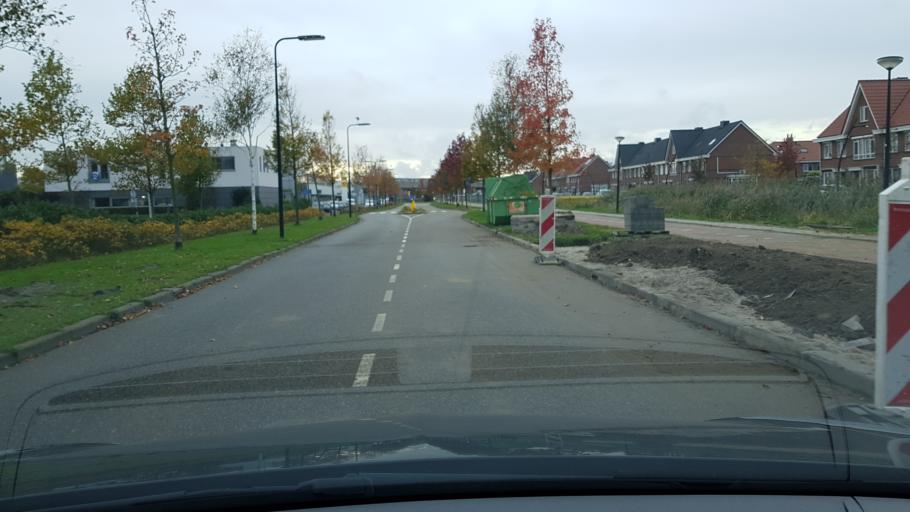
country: NL
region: South Holland
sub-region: Gemeente Spijkenisse
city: Spijkenisse
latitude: 51.8503
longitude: 4.3421
